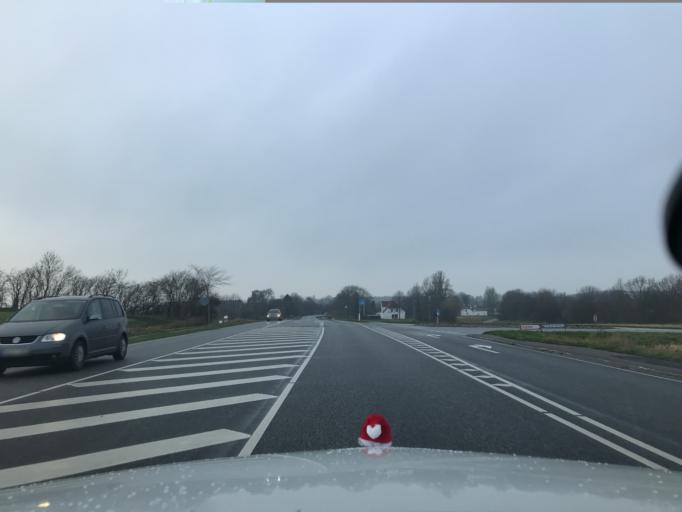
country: DK
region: South Denmark
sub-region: Sonderborg Kommune
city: Dybbol
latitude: 54.9090
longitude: 9.7228
